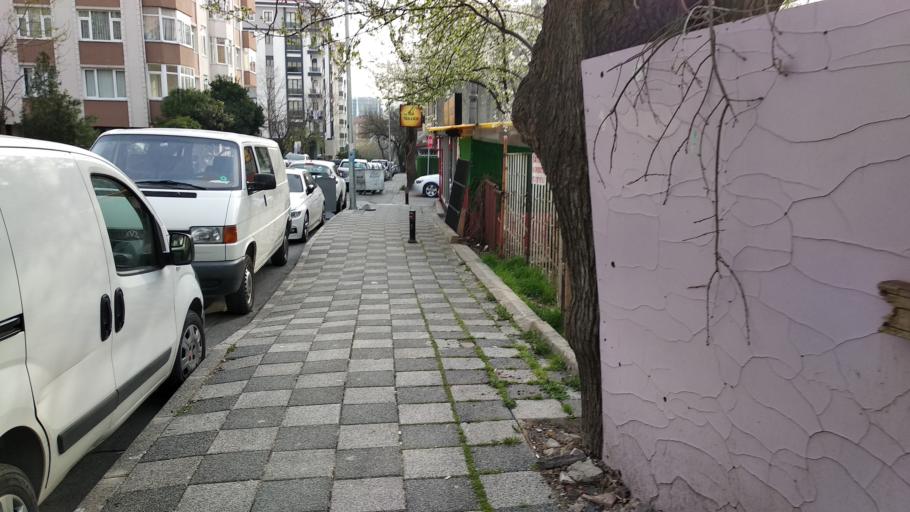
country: TR
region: Istanbul
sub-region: Atasehir
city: Atasehir
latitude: 40.9727
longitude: 29.1147
